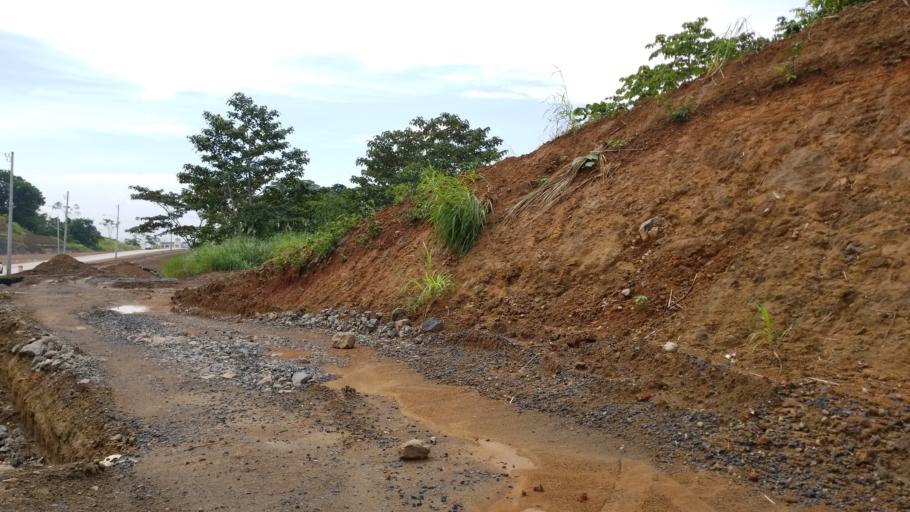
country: PA
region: Panama
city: Las Cumbres
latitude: 9.1042
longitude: -79.5291
